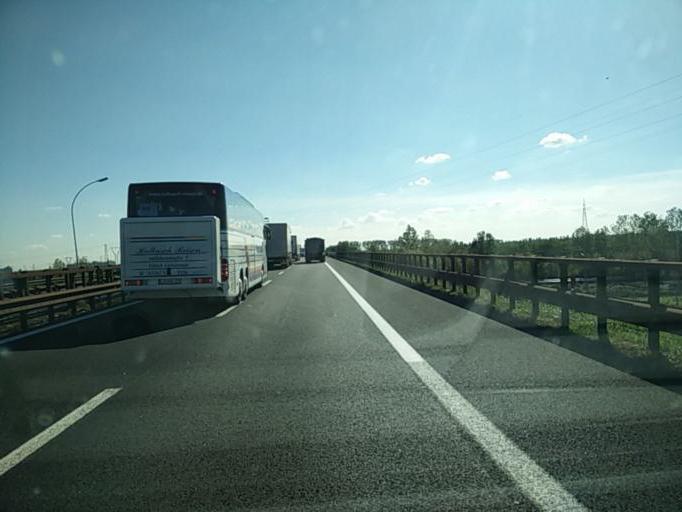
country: IT
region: Veneto
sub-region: Provincia di Verona
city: Caselle
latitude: 45.4285
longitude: 10.9088
